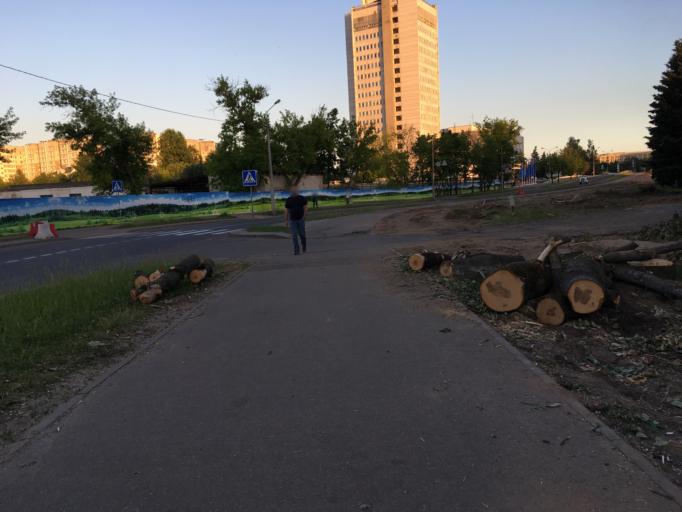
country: BY
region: Minsk
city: Minsk
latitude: 53.9254
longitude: 27.6280
